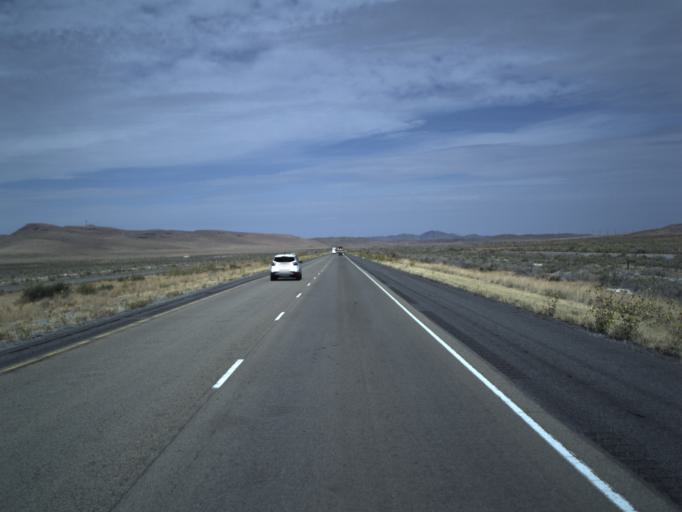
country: US
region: Utah
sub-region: Tooele County
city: Grantsville
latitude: 40.7765
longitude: -112.8061
